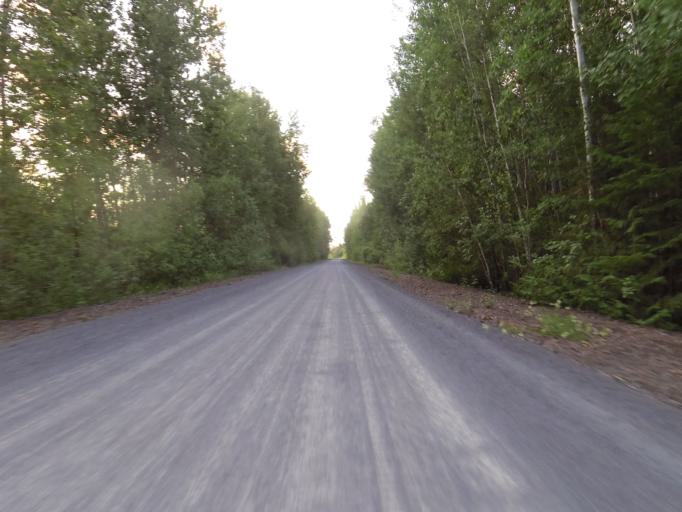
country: CA
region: Ontario
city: Arnprior
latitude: 45.3922
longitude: -76.3223
